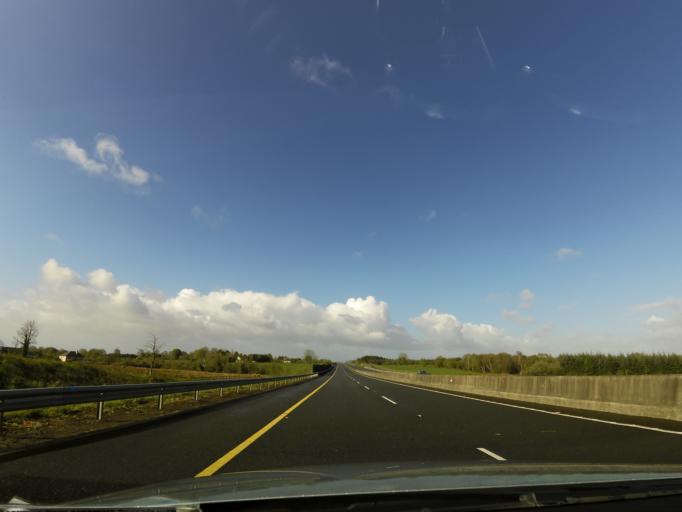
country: IE
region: Munster
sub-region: North Tipperary
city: Newport
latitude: 52.7426
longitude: -8.4394
